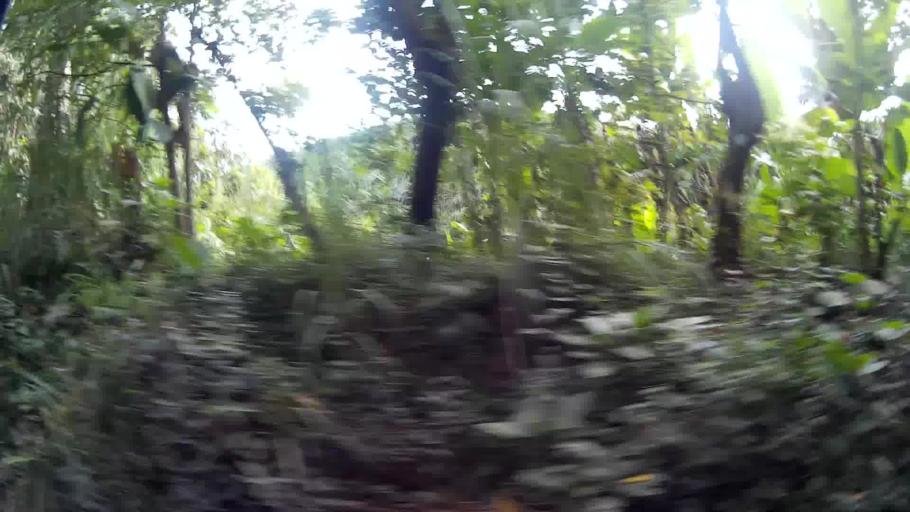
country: CO
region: Valle del Cauca
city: Ulloa
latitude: 4.7378
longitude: -75.7418
